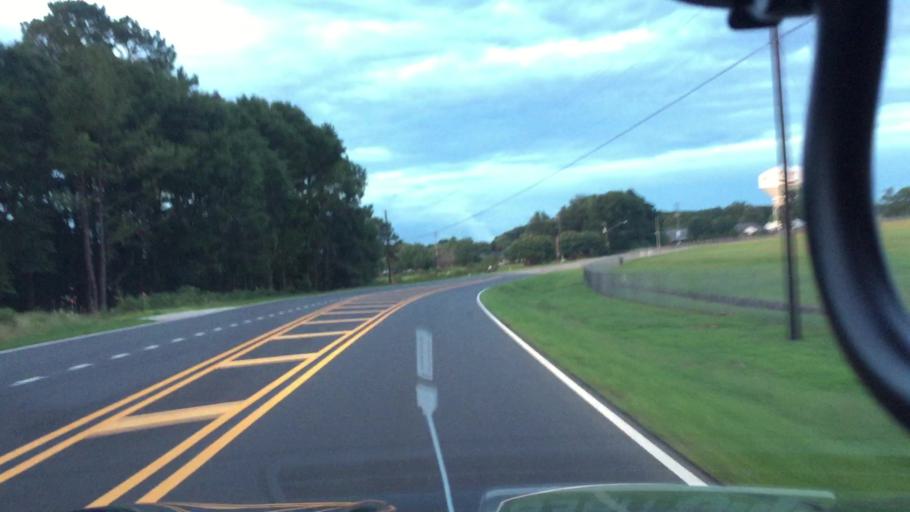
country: US
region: Alabama
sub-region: Coffee County
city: Enterprise
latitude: 31.3665
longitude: -85.8525
